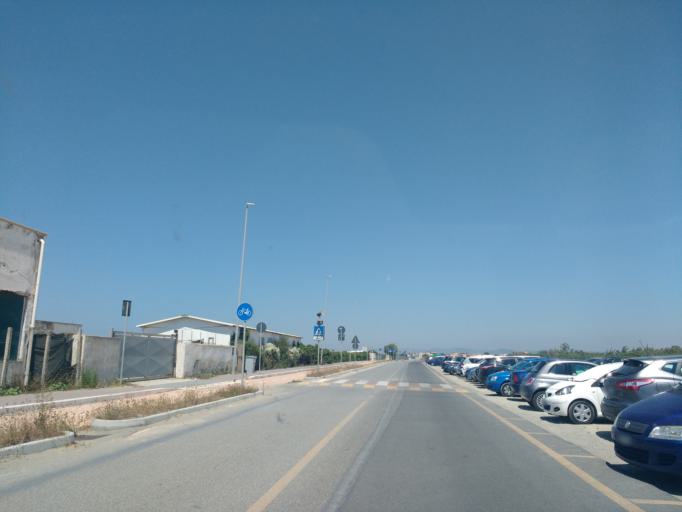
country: IT
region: Latium
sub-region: Citta metropolitana di Roma Capitale
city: Passo Oscuro
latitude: 41.8886
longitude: 12.1681
